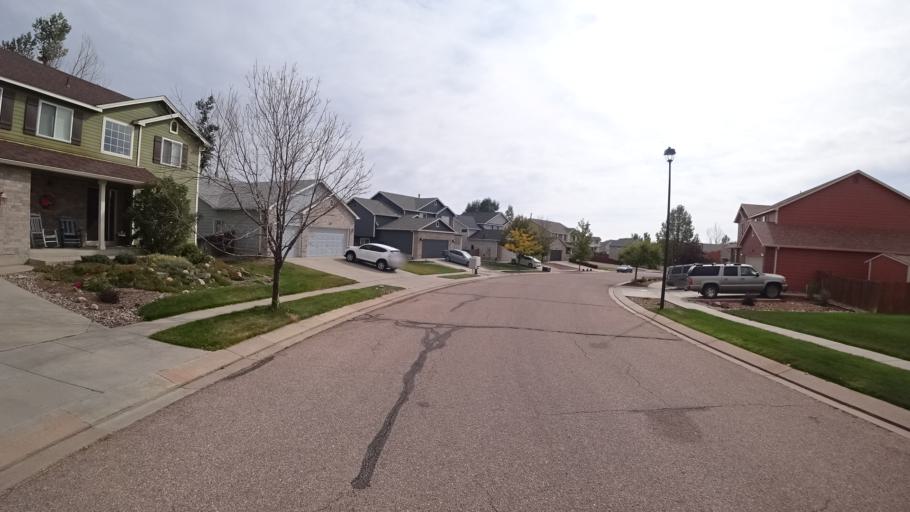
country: US
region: Colorado
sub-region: El Paso County
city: Cimarron Hills
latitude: 38.9171
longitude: -104.7085
